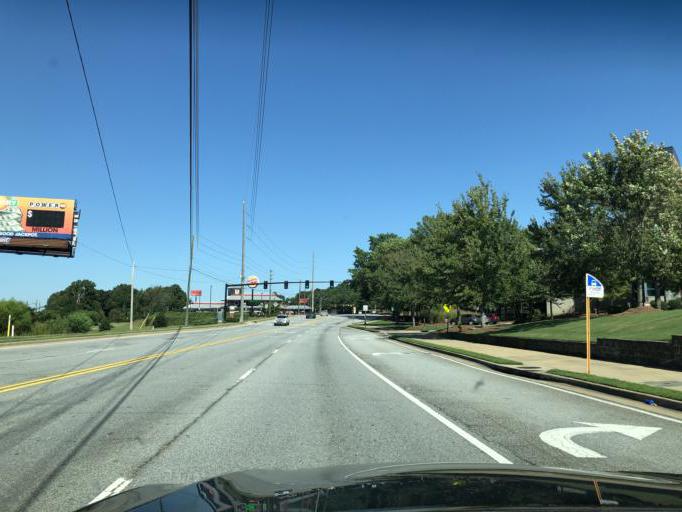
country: US
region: Georgia
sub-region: Muscogee County
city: Columbus
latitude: 32.5057
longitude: -84.9430
